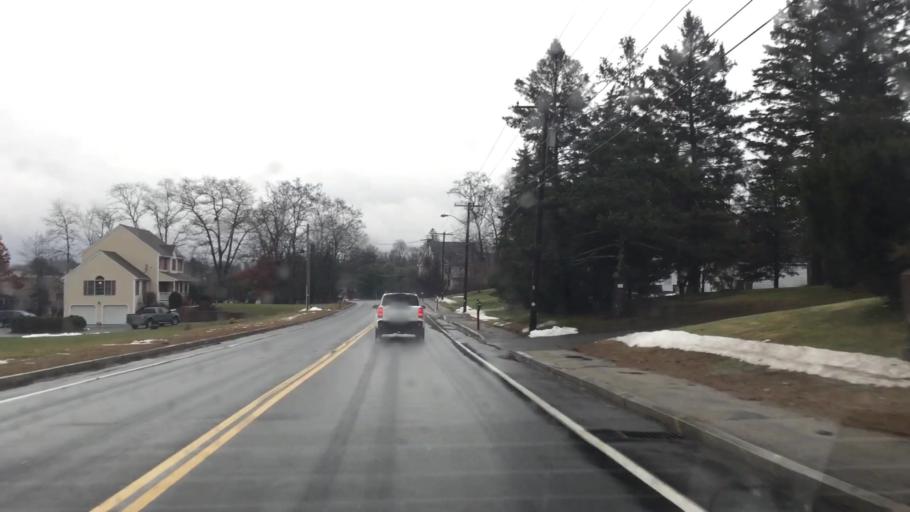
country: US
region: New Hampshire
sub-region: Rockingham County
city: Salem
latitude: 42.7570
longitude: -71.2165
